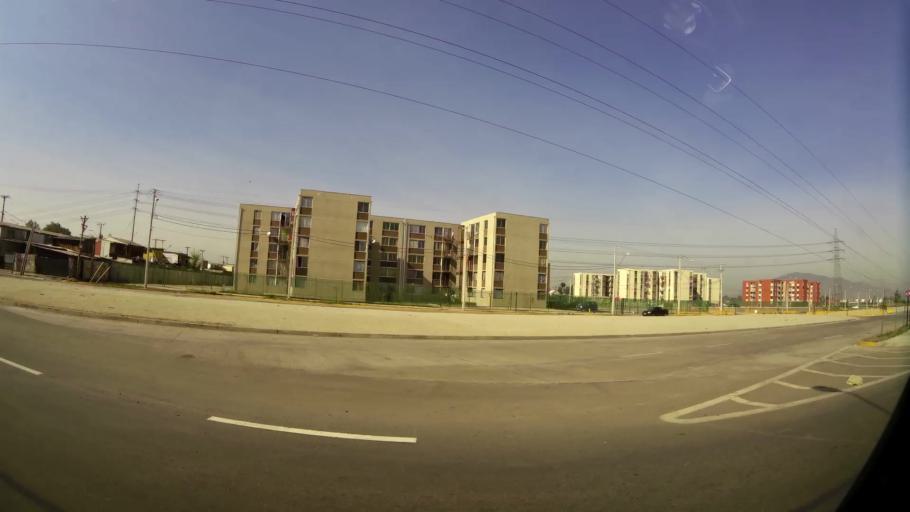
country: CL
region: Santiago Metropolitan
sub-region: Provincia de Santiago
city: Lo Prado
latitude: -33.4230
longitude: -70.7593
